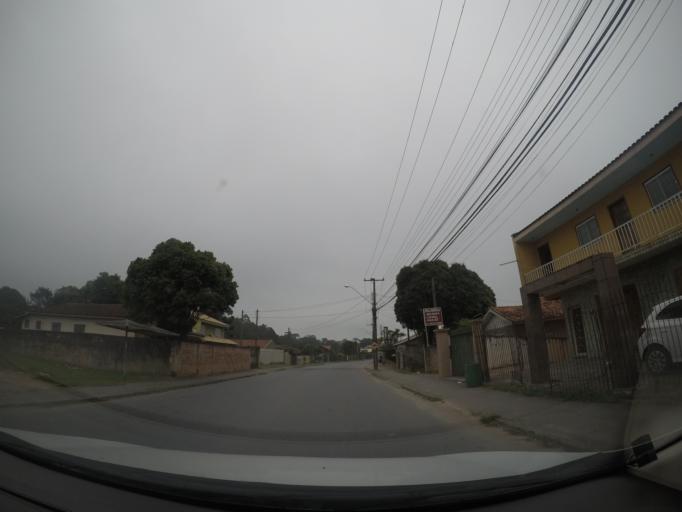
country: BR
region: Parana
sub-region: Almirante Tamandare
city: Almirante Tamandare
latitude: -25.3459
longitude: -49.2602
